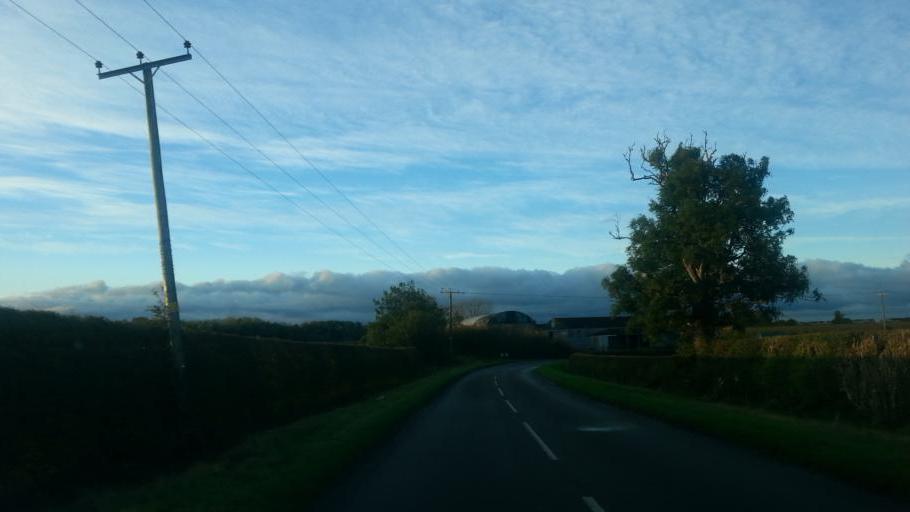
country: GB
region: England
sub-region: Nottinghamshire
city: Farndon
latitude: 53.0064
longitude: -0.8167
